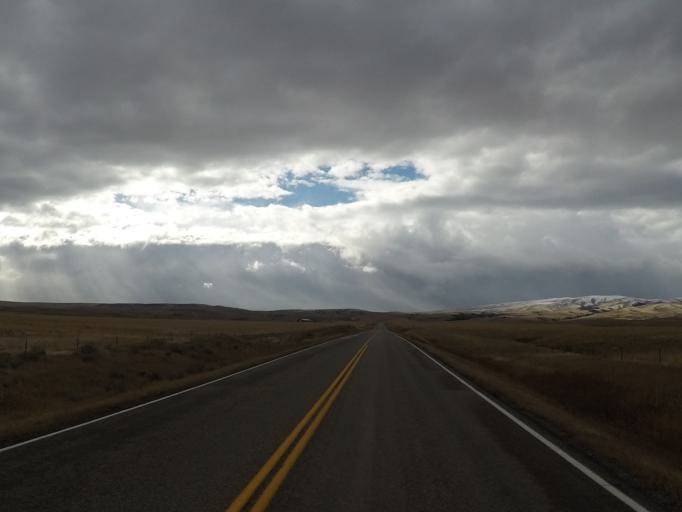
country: US
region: Montana
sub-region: Meagher County
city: White Sulphur Springs
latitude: 46.4084
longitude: -110.9315
